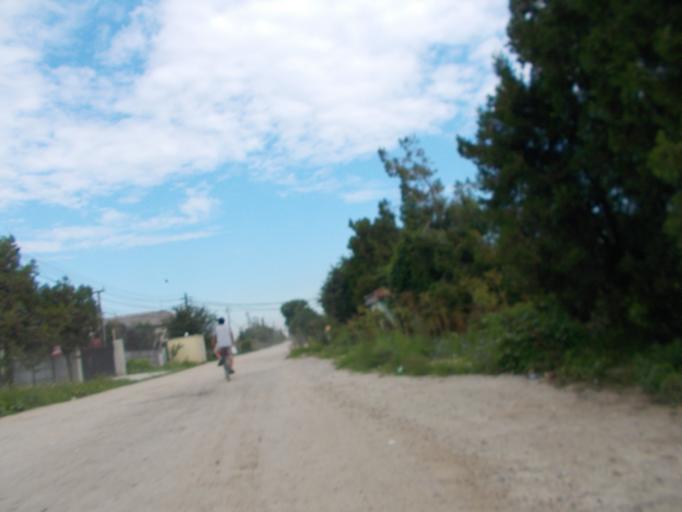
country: RO
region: Ilfov
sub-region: Comuna Jilava
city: Jilava
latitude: 44.3266
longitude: 26.0731
